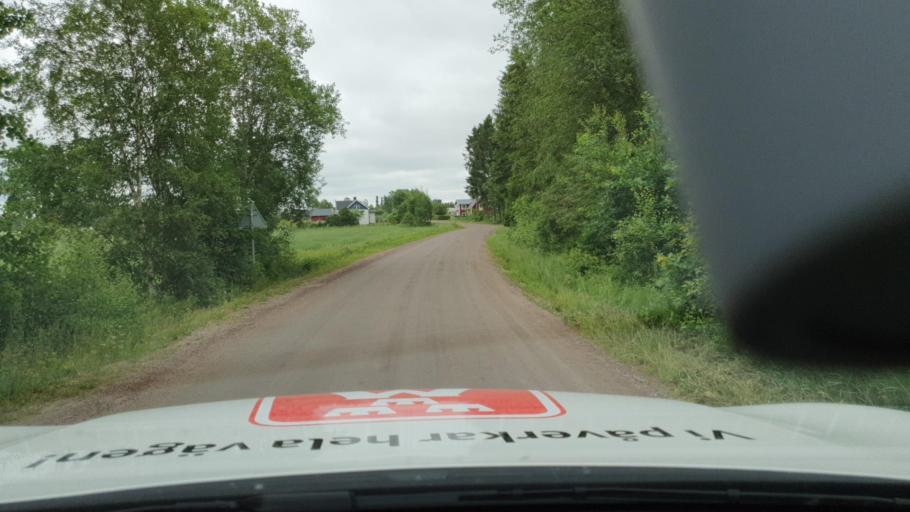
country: SE
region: Vaestra Goetaland
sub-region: Tidaholms Kommun
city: Olofstorp
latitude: 58.3559
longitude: 14.0398
